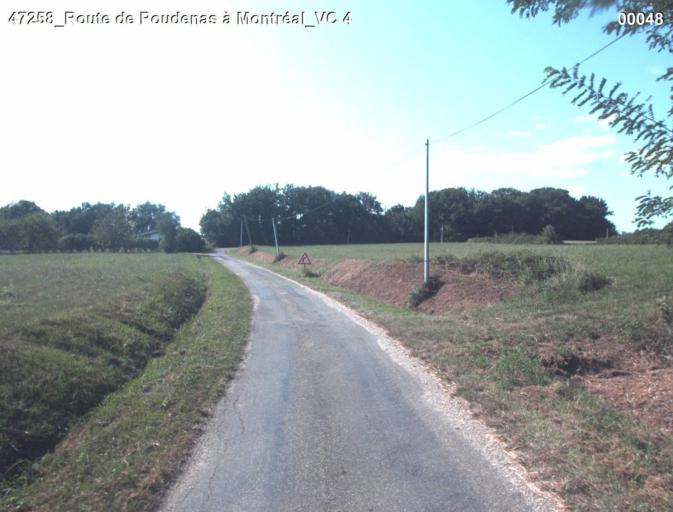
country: FR
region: Midi-Pyrenees
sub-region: Departement du Gers
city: Montreal
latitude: 44.0055
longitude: 0.1823
